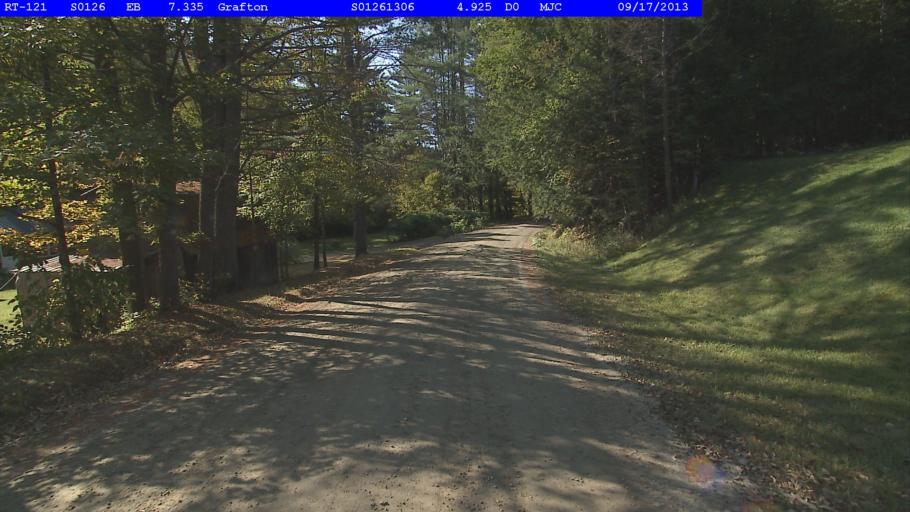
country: US
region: Vermont
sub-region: Windsor County
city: Chester
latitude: 43.1803
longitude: -72.6116
